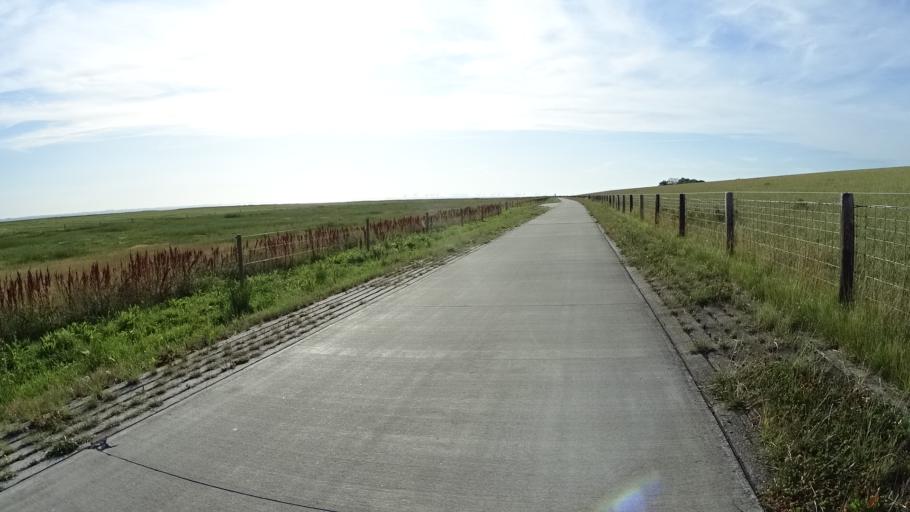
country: DE
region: Lower Saxony
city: Butjadingen
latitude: 53.6047
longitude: 8.3389
